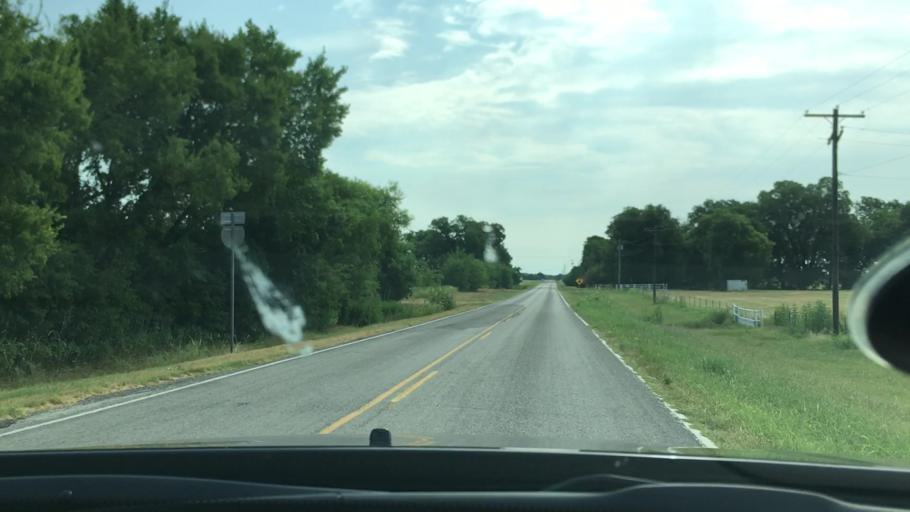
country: US
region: Oklahoma
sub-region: Carter County
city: Ardmore
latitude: 34.3327
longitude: -97.1483
